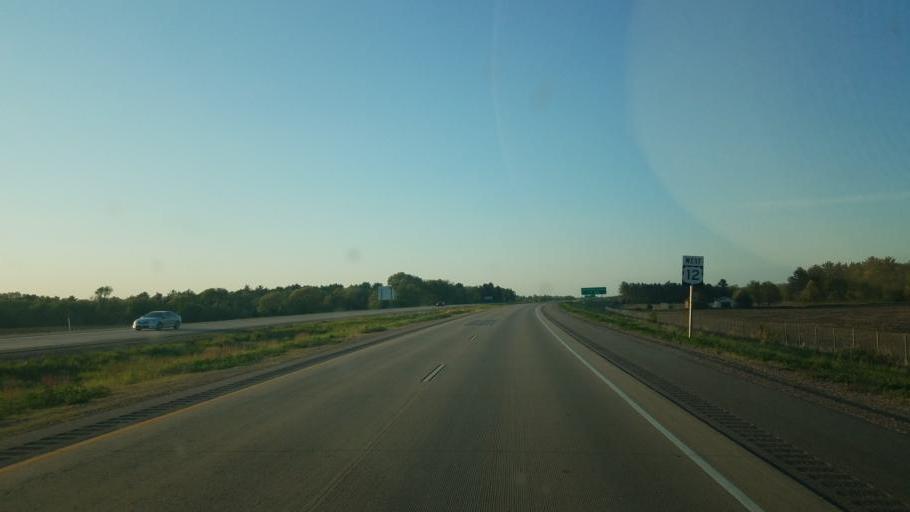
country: US
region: Wisconsin
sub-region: Sauk County
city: West Baraboo
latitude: 43.5225
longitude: -89.7867
